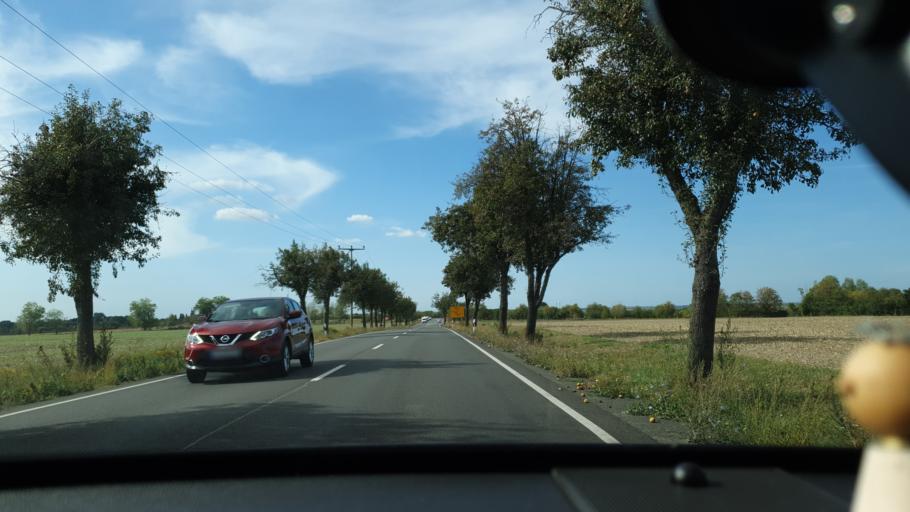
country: DE
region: Saxony
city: Krostitz
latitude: 51.4593
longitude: 12.4775
